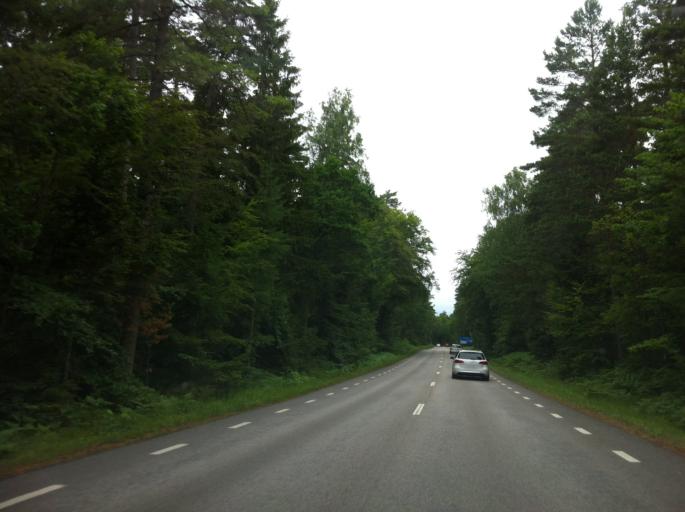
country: SE
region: Kalmar
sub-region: Borgholms Kommun
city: Borgholm
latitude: 57.2656
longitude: 17.0289
